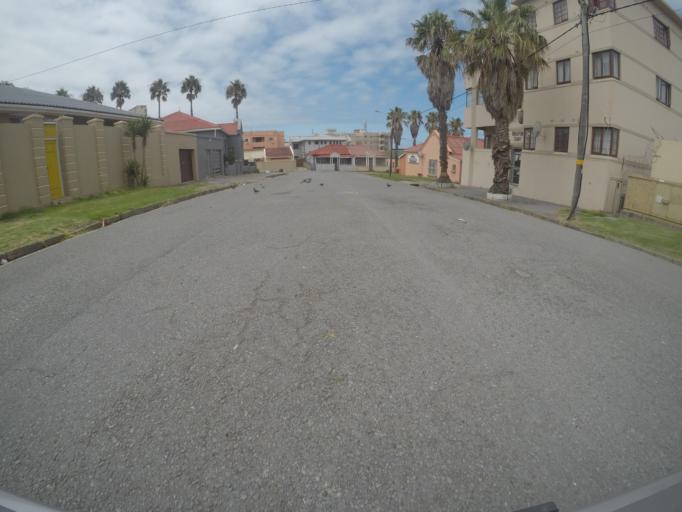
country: ZA
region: Eastern Cape
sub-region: Buffalo City Metropolitan Municipality
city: East London
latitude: -33.0202
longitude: 27.9166
